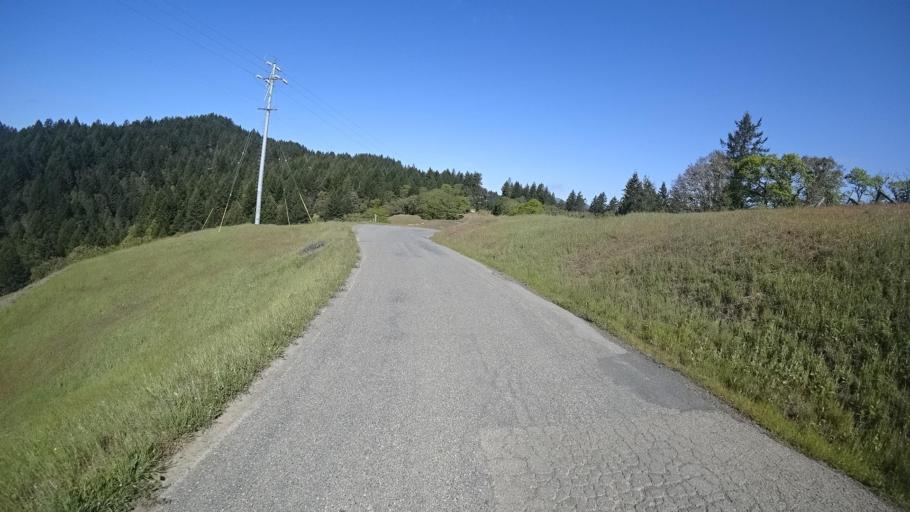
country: US
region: California
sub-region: Humboldt County
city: Redway
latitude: 40.0614
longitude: -123.6422
